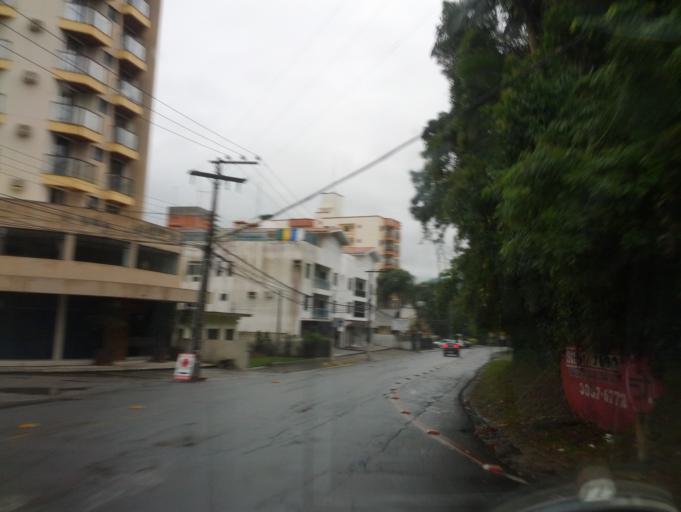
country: BR
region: Santa Catarina
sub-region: Blumenau
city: Blumenau
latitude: -26.9109
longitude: -49.0827
